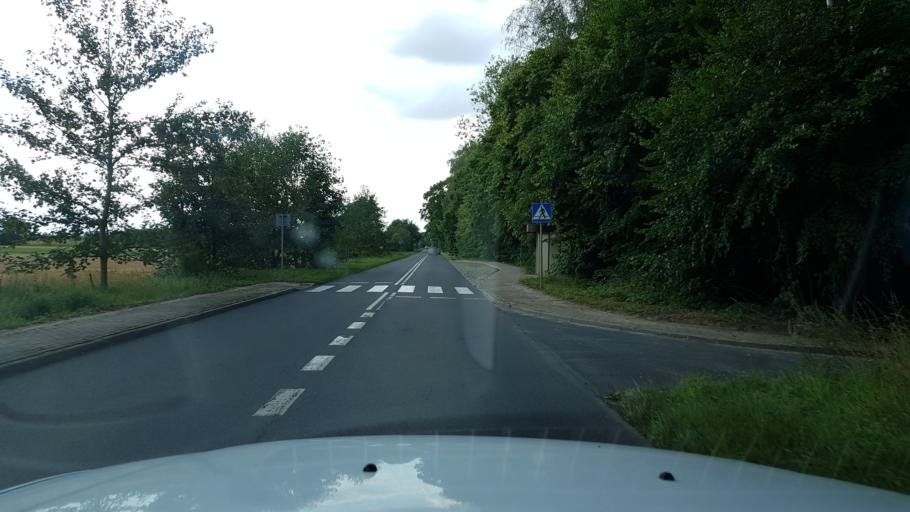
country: PL
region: West Pomeranian Voivodeship
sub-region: Powiat kamienski
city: Kamien Pomorski
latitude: 54.0009
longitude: 14.8348
